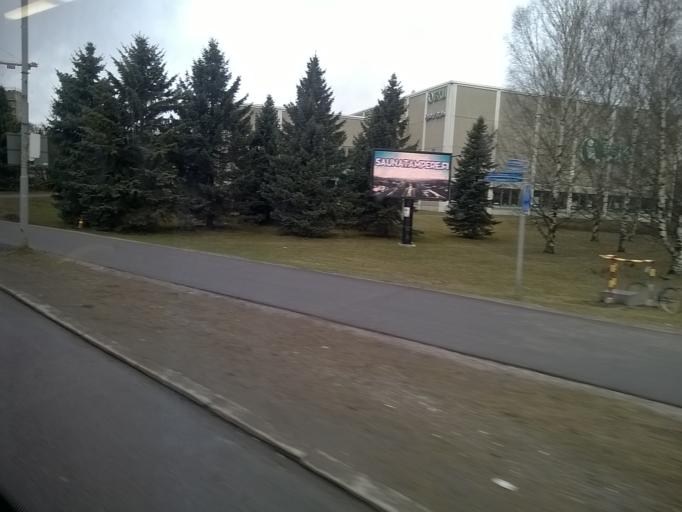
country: FI
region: Pirkanmaa
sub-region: Tampere
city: Tampere
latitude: 61.4934
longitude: 23.8211
